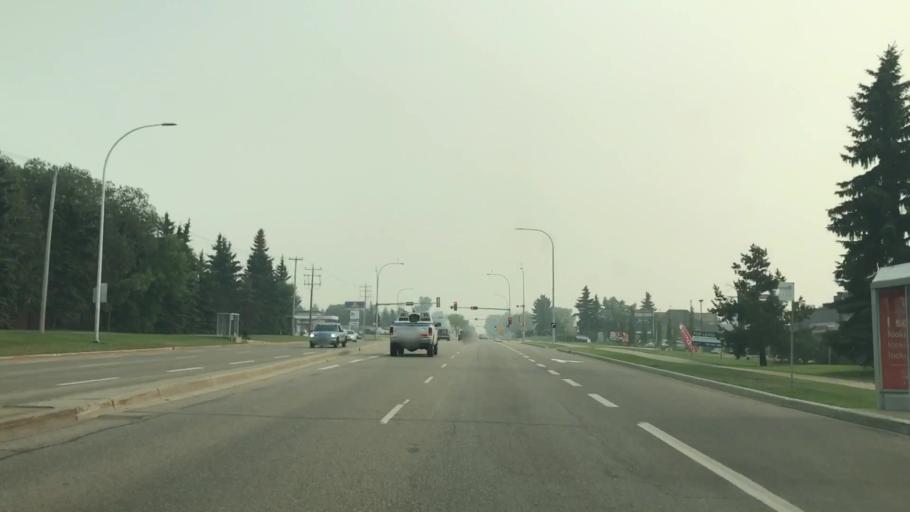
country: CA
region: Alberta
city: Sherwood Park
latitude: 53.5391
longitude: -113.3202
